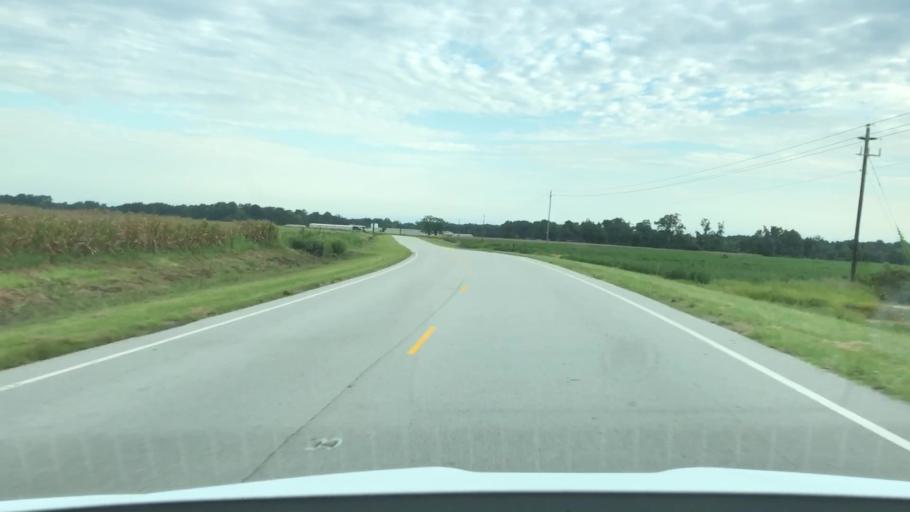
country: US
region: North Carolina
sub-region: Jones County
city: Trenton
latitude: 35.0487
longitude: -77.3530
